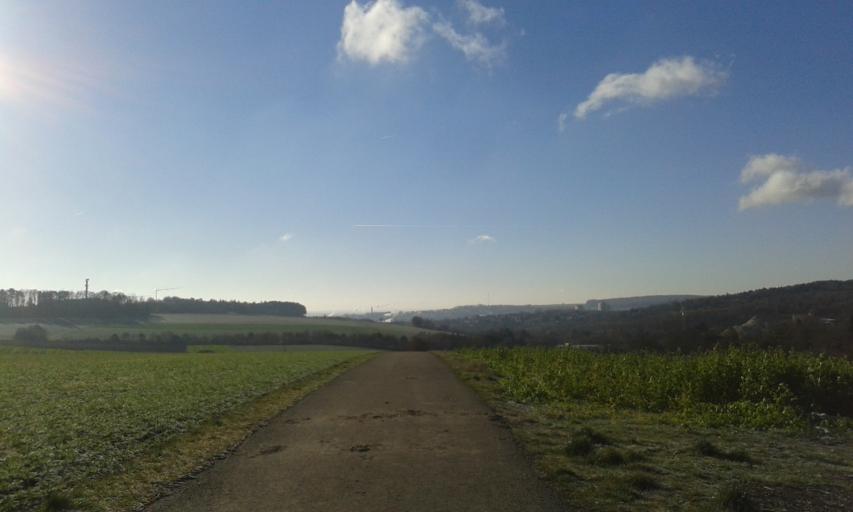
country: DE
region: Baden-Wuerttemberg
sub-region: Tuebingen Region
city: Ulm
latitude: 48.4308
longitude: 9.9789
